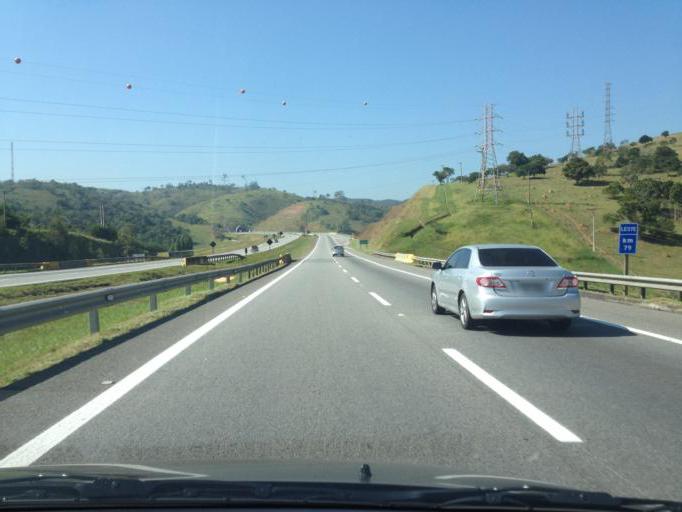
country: BR
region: Sao Paulo
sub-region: Jacarei
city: Jacarei
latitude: -23.3422
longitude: -45.9648
